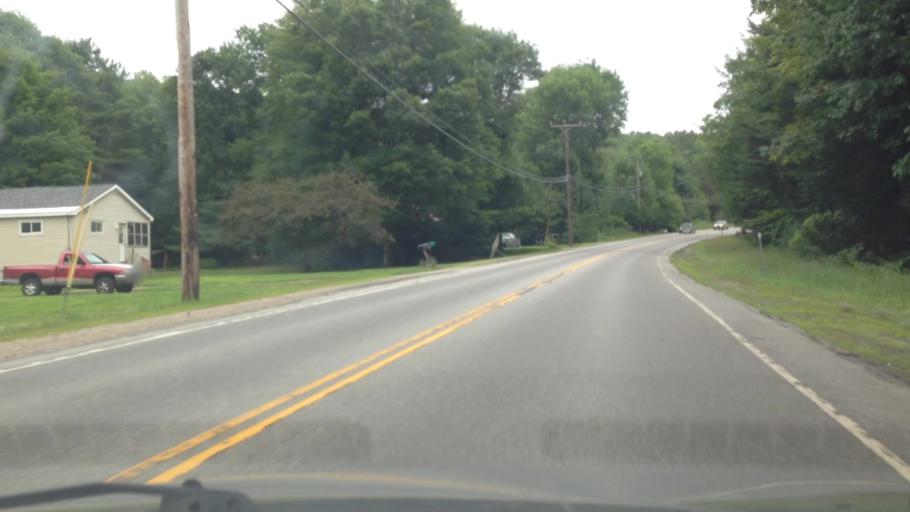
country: US
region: New Hampshire
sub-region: Cheshire County
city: Marlborough
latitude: 42.9165
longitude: -72.2306
